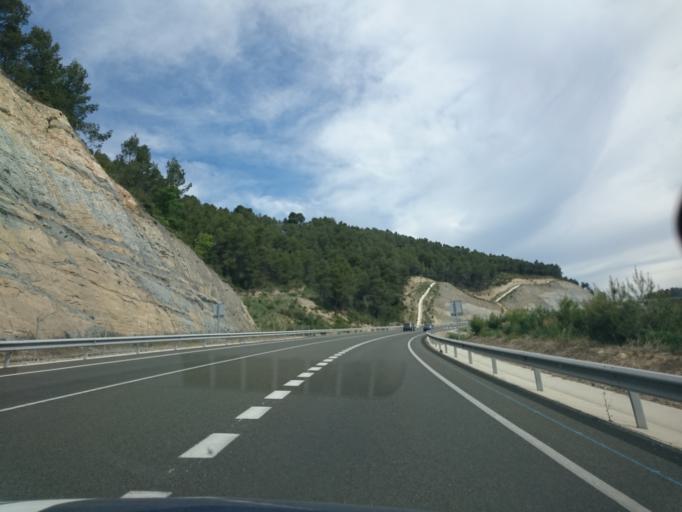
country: ES
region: Catalonia
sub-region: Provincia de Barcelona
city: Castelloli
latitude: 41.6162
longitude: 1.6807
